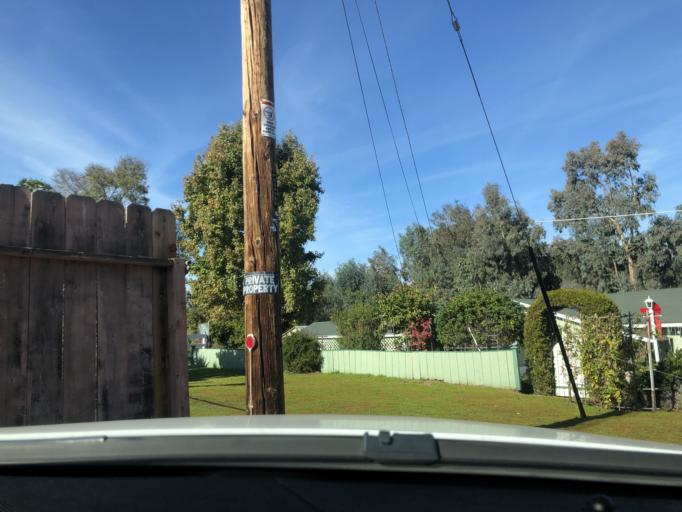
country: US
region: California
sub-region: San Diego County
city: Escondido
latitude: 33.0878
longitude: -117.0868
